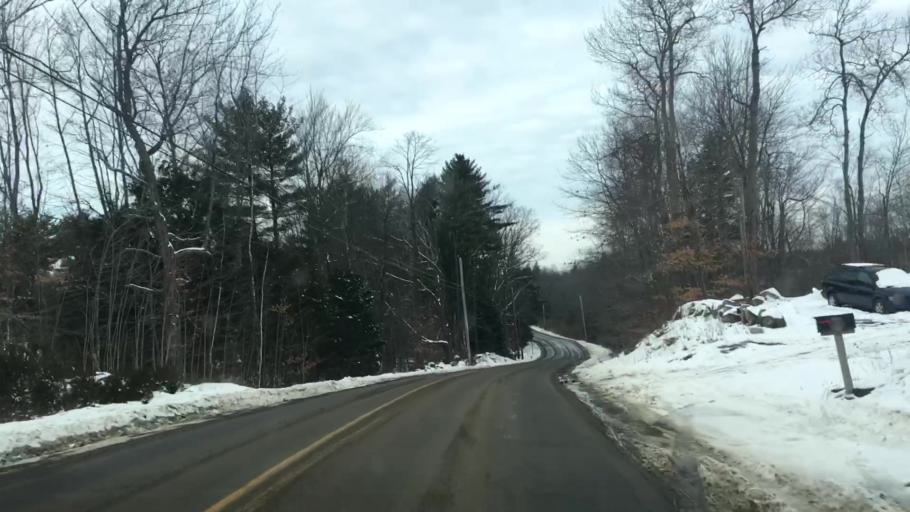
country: US
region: Maine
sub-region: Kennebec County
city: Chelsea
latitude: 44.2582
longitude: -69.6441
